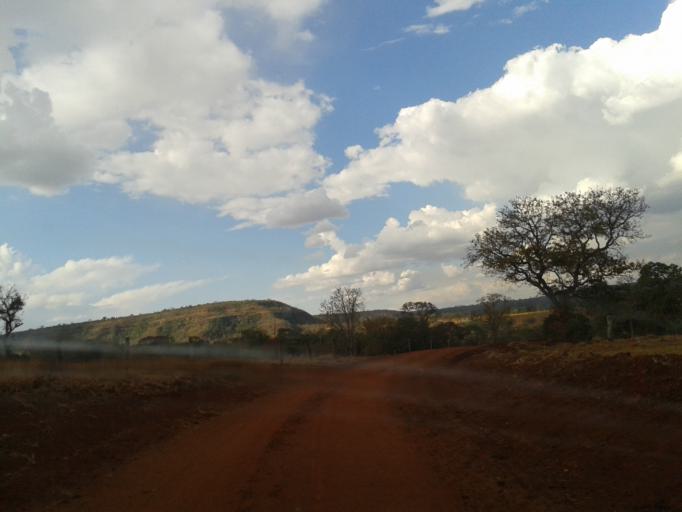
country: BR
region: Minas Gerais
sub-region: Santa Vitoria
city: Santa Vitoria
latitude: -19.1695
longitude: -49.9597
